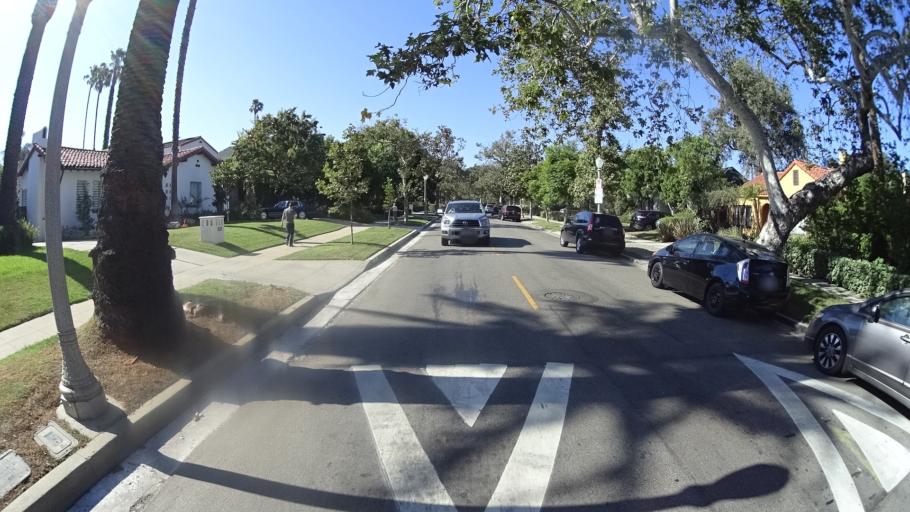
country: US
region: California
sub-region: Los Angeles County
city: Hollywood
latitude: 34.0799
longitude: -118.3295
